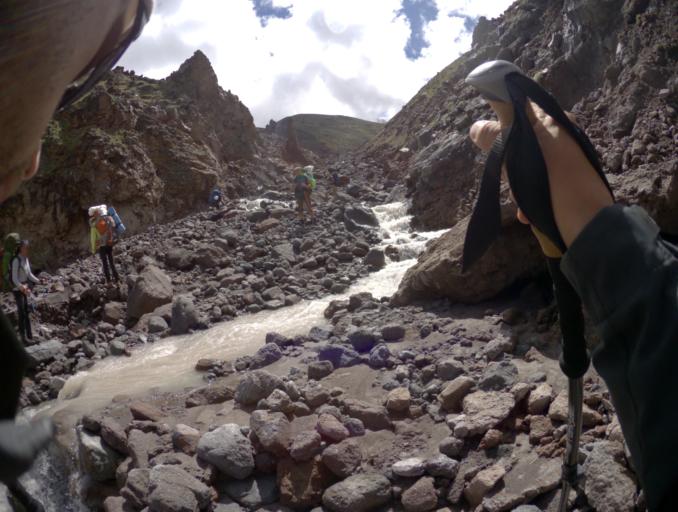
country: RU
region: Kabardino-Balkariya
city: Terskol
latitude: 43.3846
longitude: 42.3671
